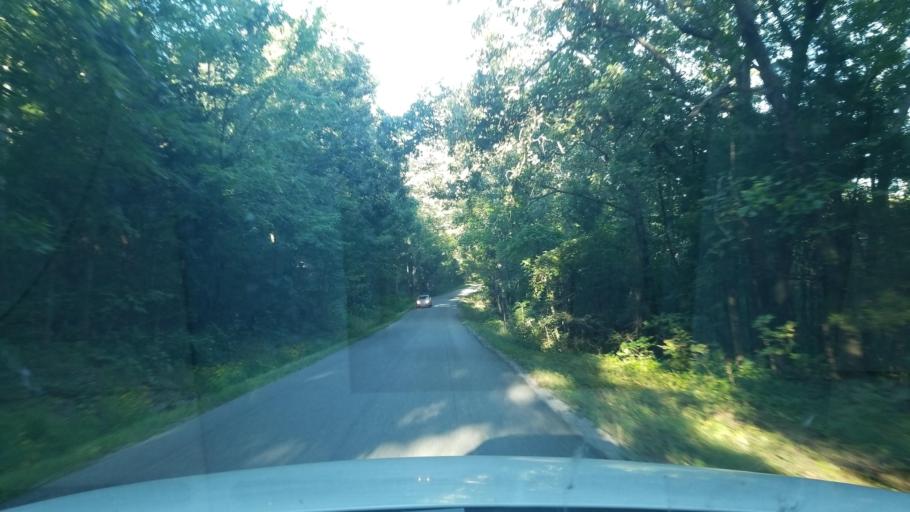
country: US
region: Illinois
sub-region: Hardin County
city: Elizabethtown
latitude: 37.6010
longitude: -88.3801
